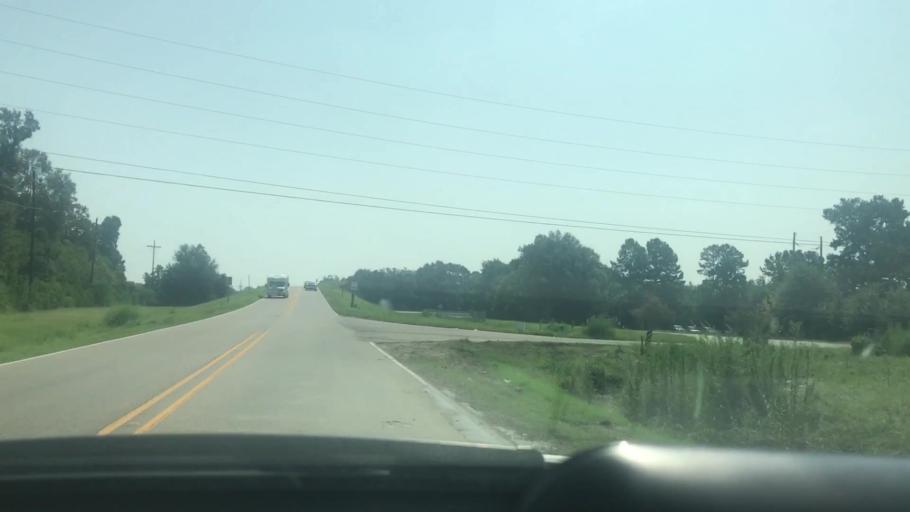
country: US
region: Louisiana
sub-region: Tangipahoa Parish
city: Hammond
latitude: 30.4755
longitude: -90.4897
